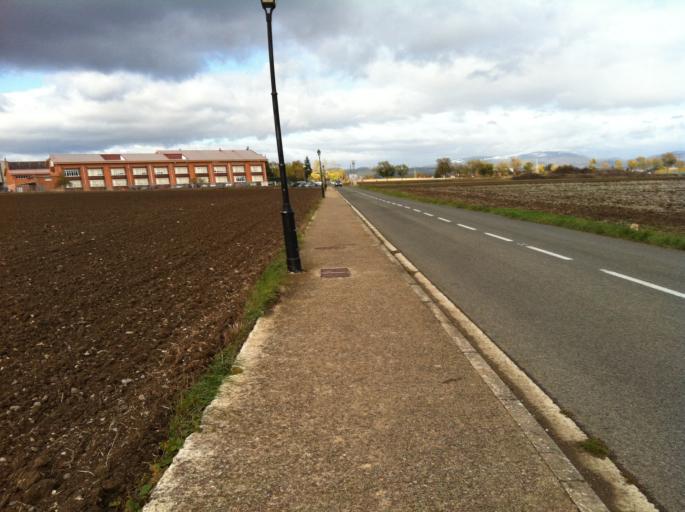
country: ES
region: Basque Country
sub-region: Provincia de Alava
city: Gasteiz / Vitoria
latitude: 42.8223
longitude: -2.6935
